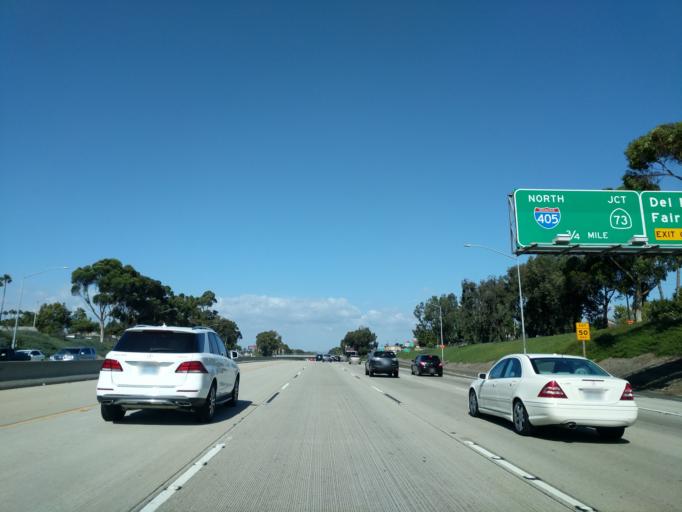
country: US
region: California
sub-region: Orange County
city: Costa Mesa
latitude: 33.6595
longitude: -117.9012
